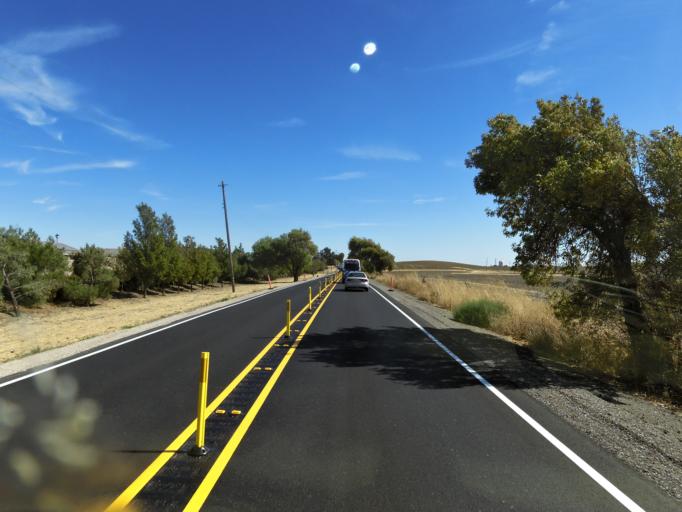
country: US
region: California
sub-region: Solano County
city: Rio Vista
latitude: 38.1773
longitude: -121.7177
